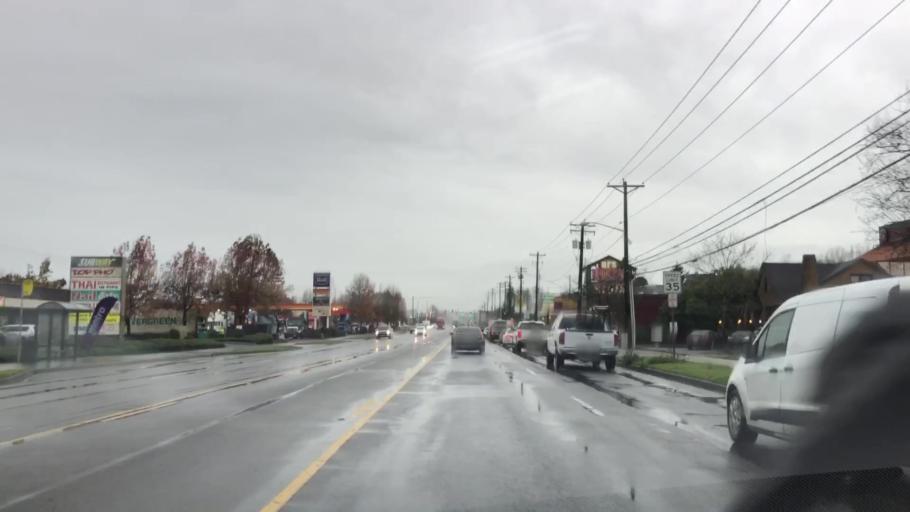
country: US
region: Washington
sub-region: Pierce County
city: Fife
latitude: 47.2431
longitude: -122.3685
